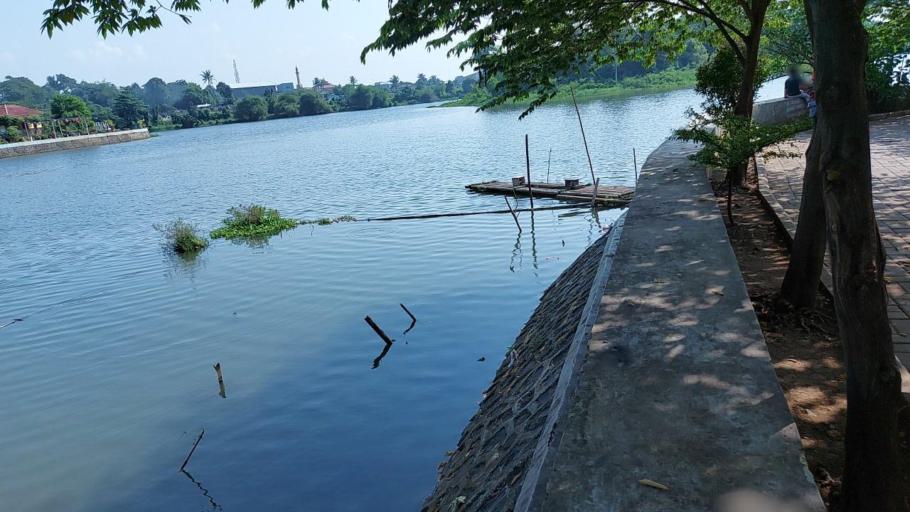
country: ID
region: West Java
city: Cibinong
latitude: -6.4721
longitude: 106.8557
